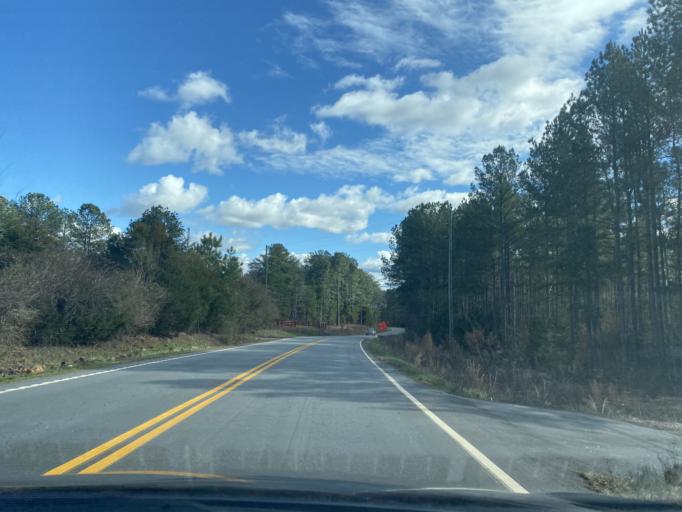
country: US
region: South Carolina
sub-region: Cherokee County
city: Gaffney
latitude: 35.0937
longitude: -81.7433
